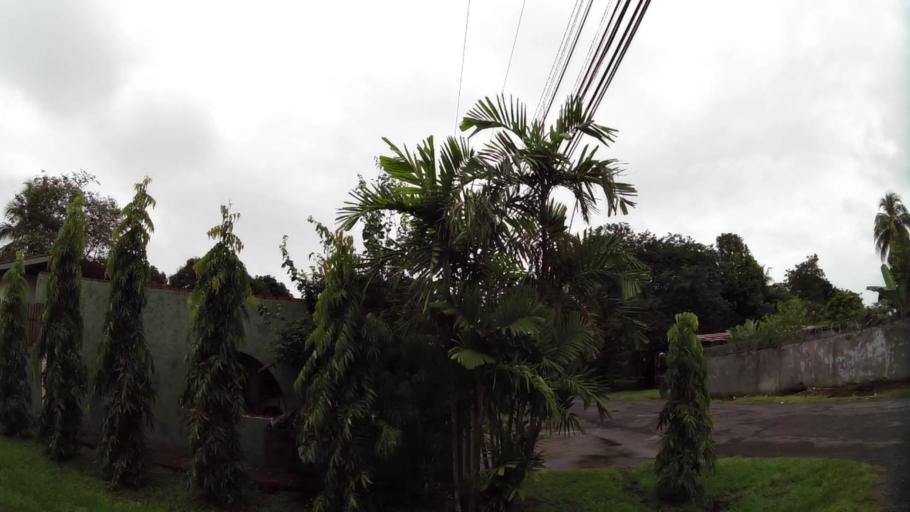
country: PA
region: Chiriqui
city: David
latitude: 8.4243
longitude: -82.4502
